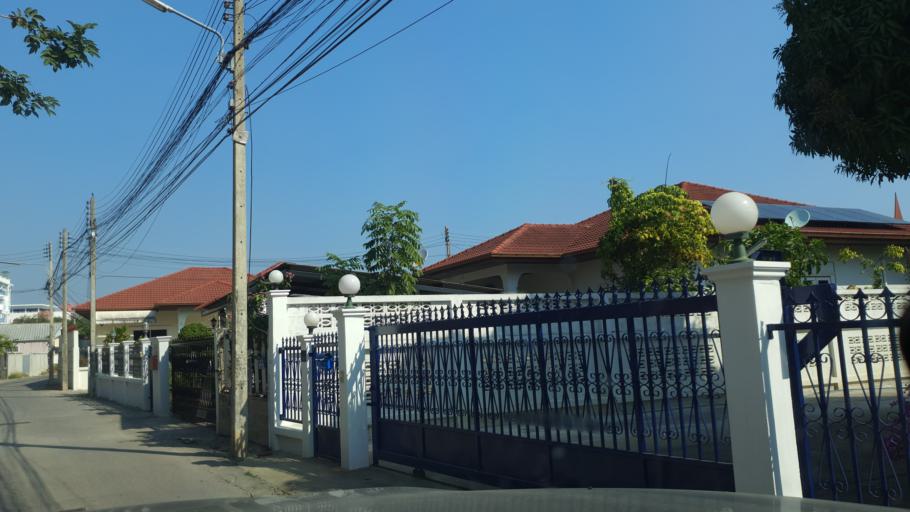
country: TH
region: Prachuap Khiri Khan
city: Hua Hin
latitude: 12.5513
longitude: 99.9549
